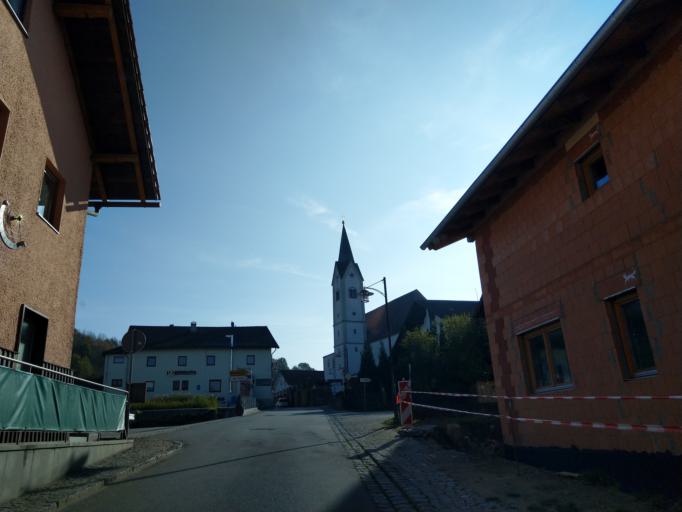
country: DE
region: Bavaria
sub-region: Lower Bavaria
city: Grattersdorf
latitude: 48.8044
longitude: 13.1513
